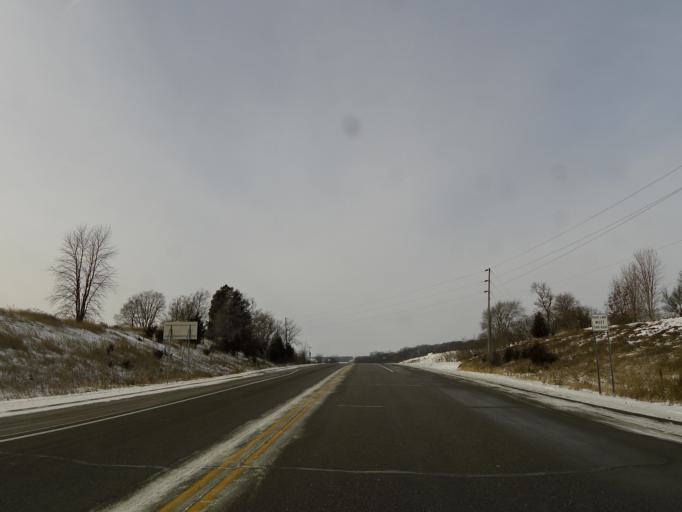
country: US
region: Minnesota
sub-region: Hennepin County
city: Saint Bonifacius
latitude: 44.9055
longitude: -93.7664
